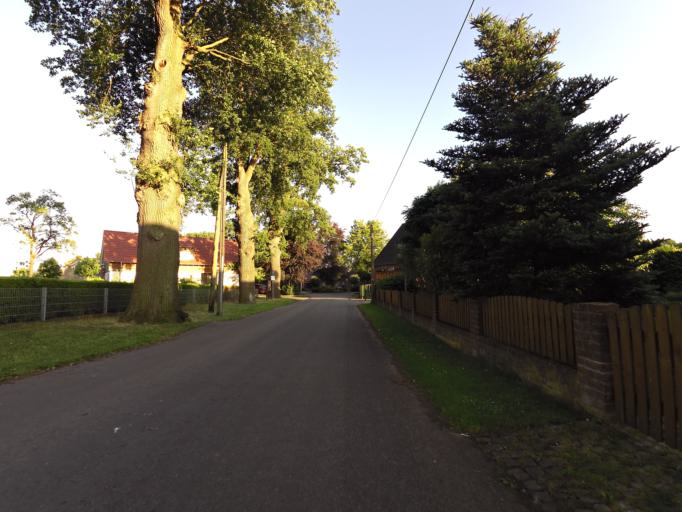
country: DE
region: North Rhine-Westphalia
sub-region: Regierungsbezirk Munster
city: Isselburg
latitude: 51.8586
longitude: 6.4348
